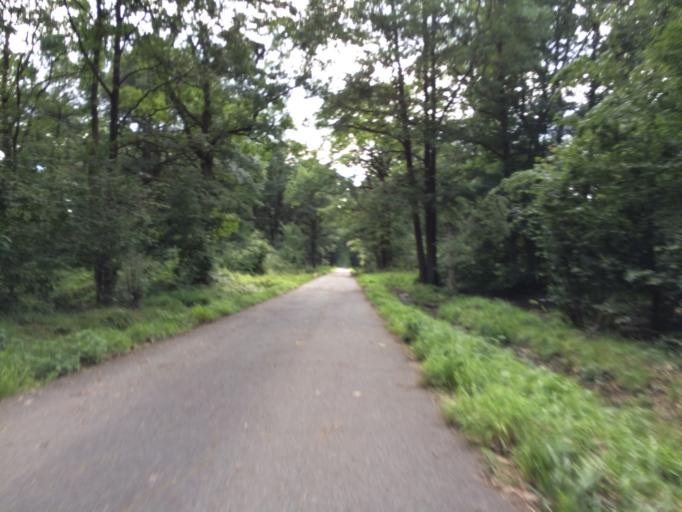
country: FR
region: Ile-de-France
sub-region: Departement de l'Essonne
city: Soisy-sur-Seine
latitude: 48.6618
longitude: 2.4540
